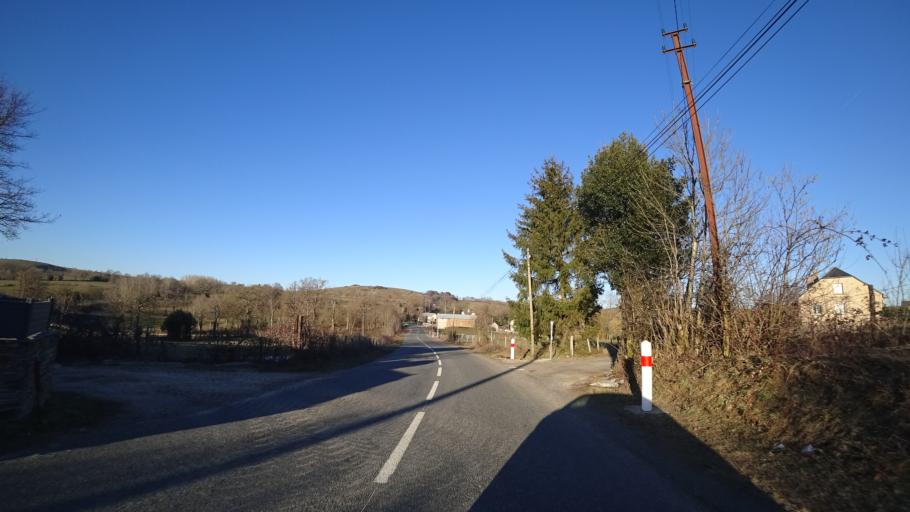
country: FR
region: Midi-Pyrenees
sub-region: Departement de l'Aveyron
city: Pont-de-Salars
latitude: 44.3277
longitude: 2.7614
